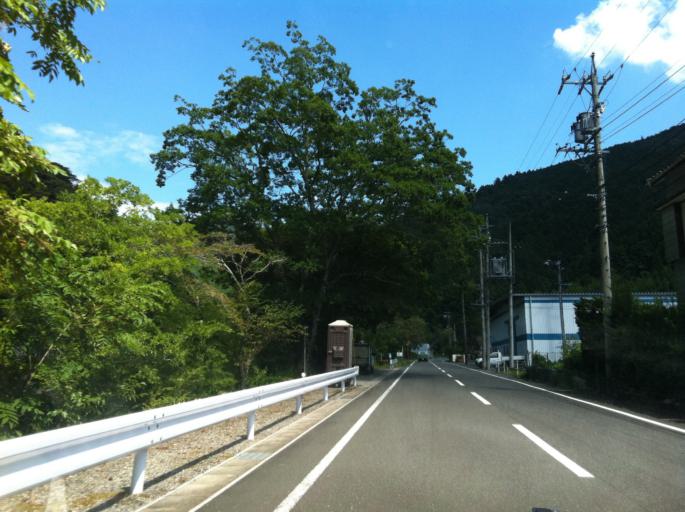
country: JP
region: Shizuoka
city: Shizuoka-shi
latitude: 35.0833
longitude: 138.2424
